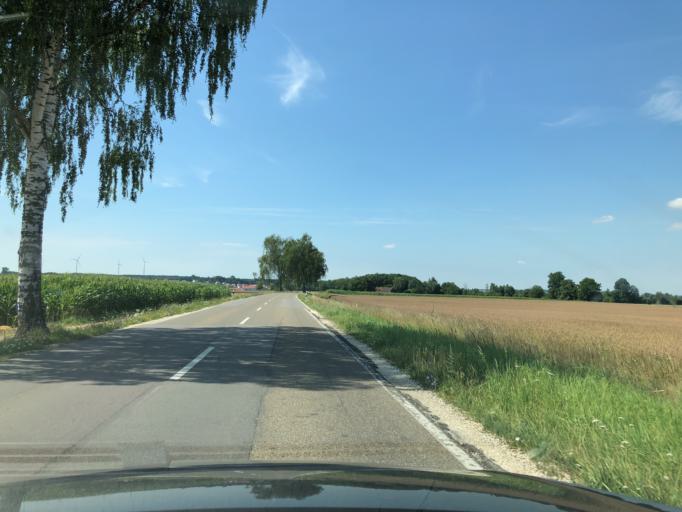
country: DE
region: Bavaria
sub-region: Swabia
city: Allmannshofen
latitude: 48.6375
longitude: 10.7672
